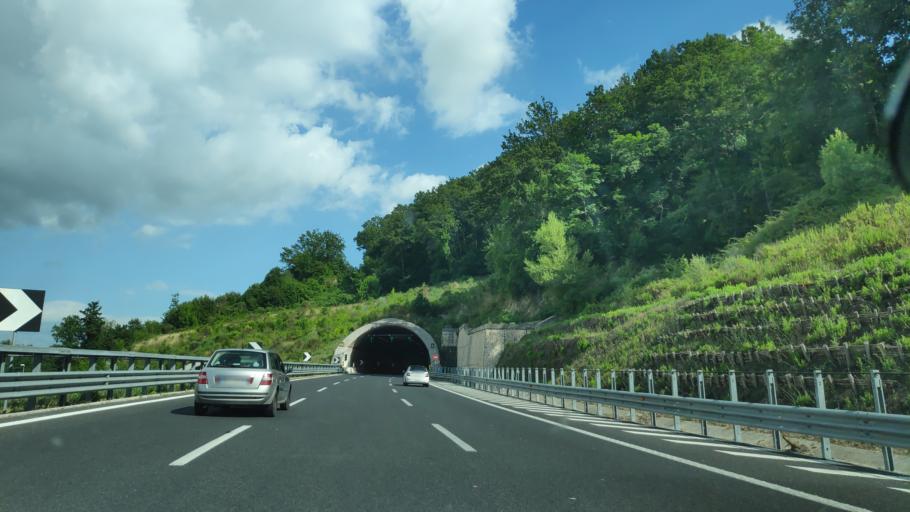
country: IT
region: Campania
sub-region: Provincia di Salerno
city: Contursi Terme
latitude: 40.6270
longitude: 15.2363
